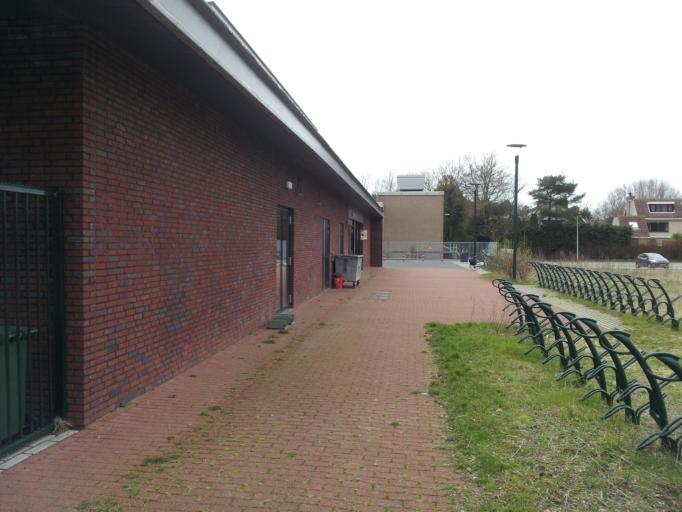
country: NL
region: South Holland
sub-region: Gemeente Wassenaar
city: Wassenaar
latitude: 52.1360
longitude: 4.3905
